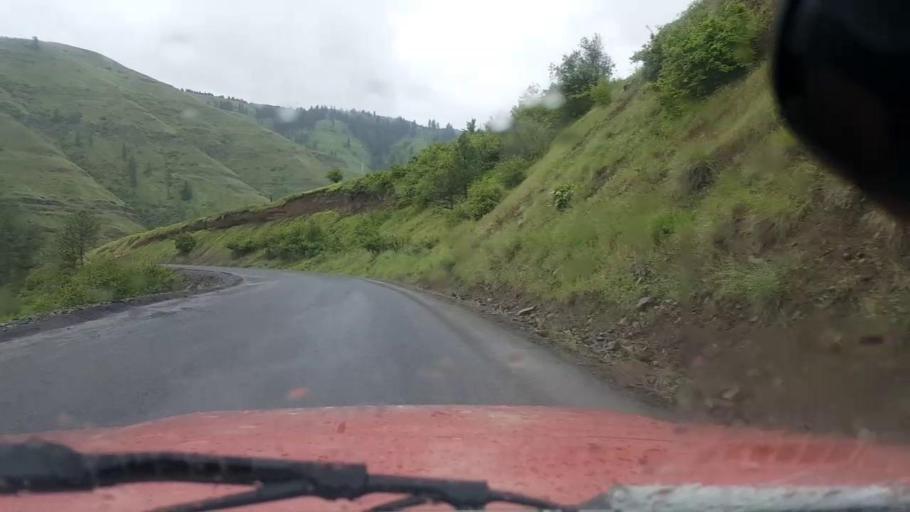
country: US
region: Washington
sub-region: Asotin County
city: Asotin
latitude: 46.0357
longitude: -117.2968
